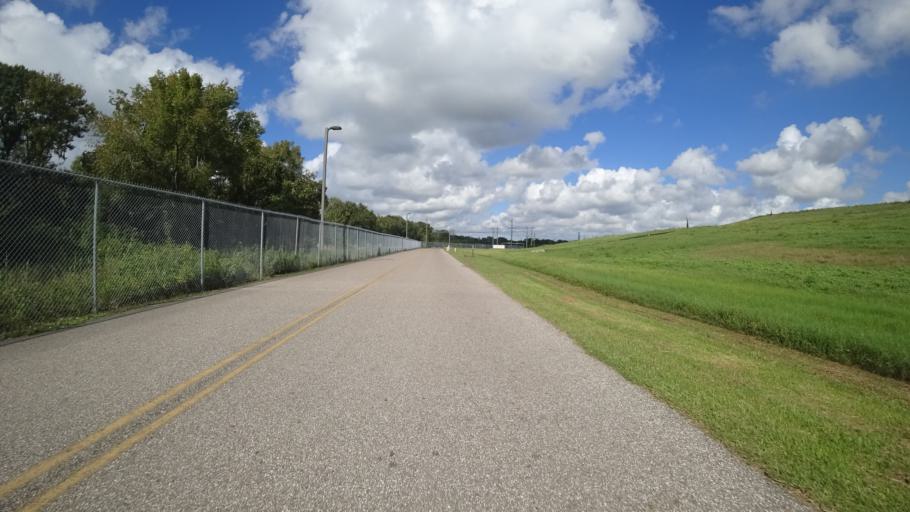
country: US
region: Florida
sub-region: Manatee County
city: Samoset
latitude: 27.4708
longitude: -82.4523
